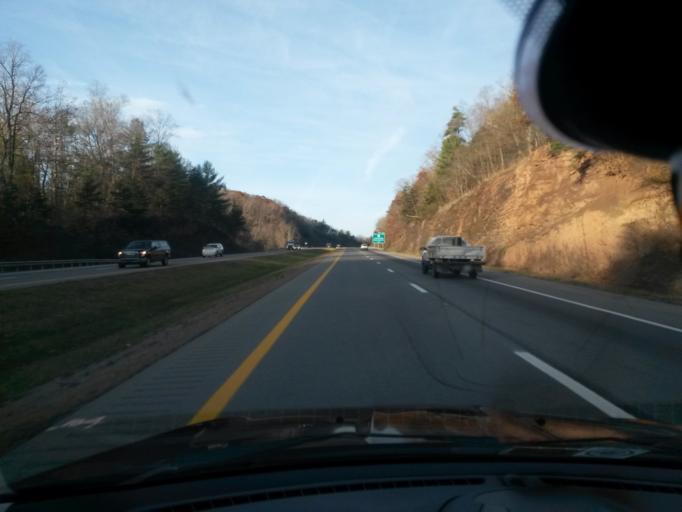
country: US
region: West Virginia
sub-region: Greenbrier County
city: Lewisburg
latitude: 37.8074
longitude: -80.4053
